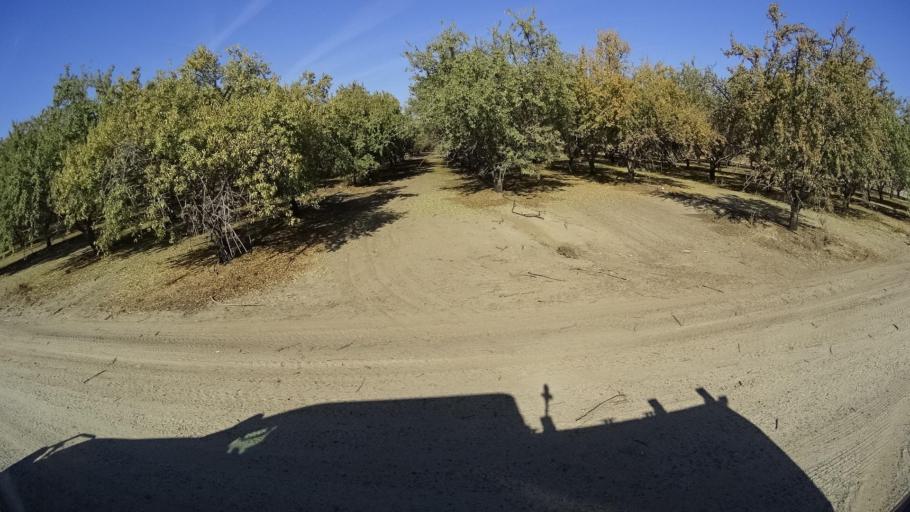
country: US
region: California
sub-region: Kern County
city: McFarland
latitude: 35.6455
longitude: -119.2431
